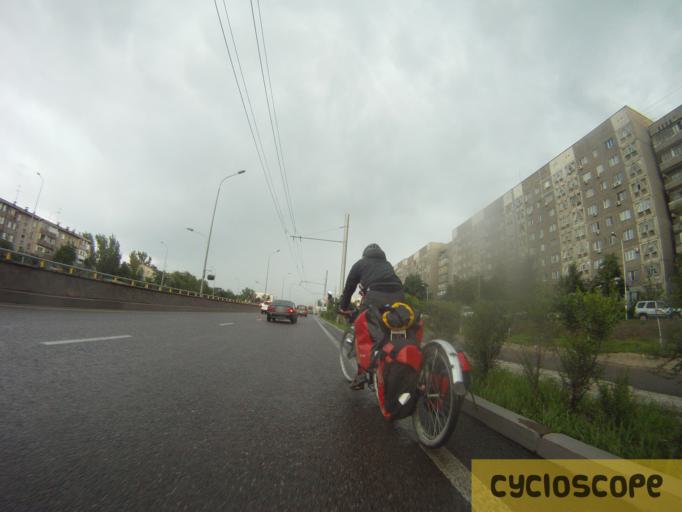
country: KZ
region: Almaty Qalasy
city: Almaty
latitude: 43.2370
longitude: 76.8401
